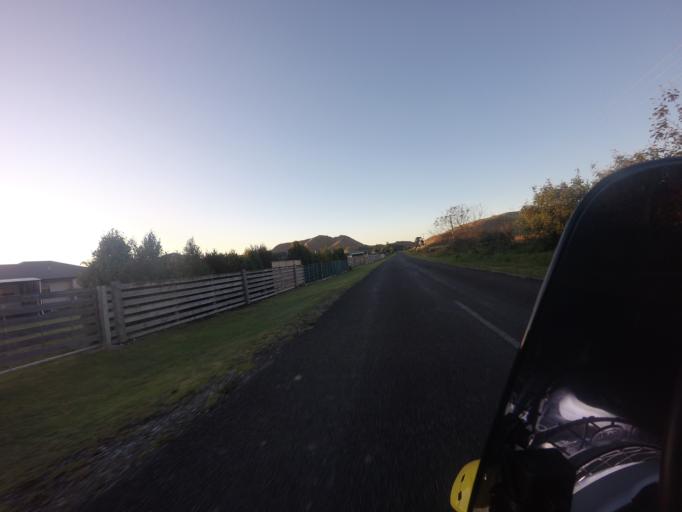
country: NZ
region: Gisborne
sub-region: Gisborne District
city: Gisborne
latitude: -38.6899
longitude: 178.0568
